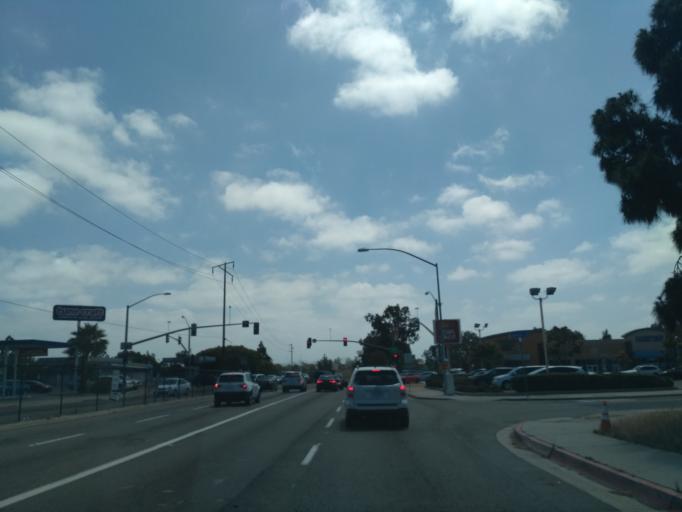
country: US
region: California
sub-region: San Diego County
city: La Jolla
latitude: 32.8116
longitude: -117.2021
